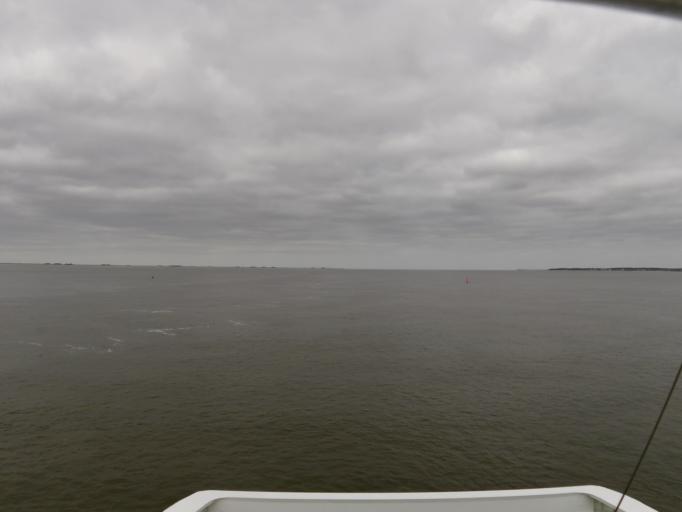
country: DE
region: Schleswig-Holstein
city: Dagebull
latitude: 54.6998
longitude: 8.6374
